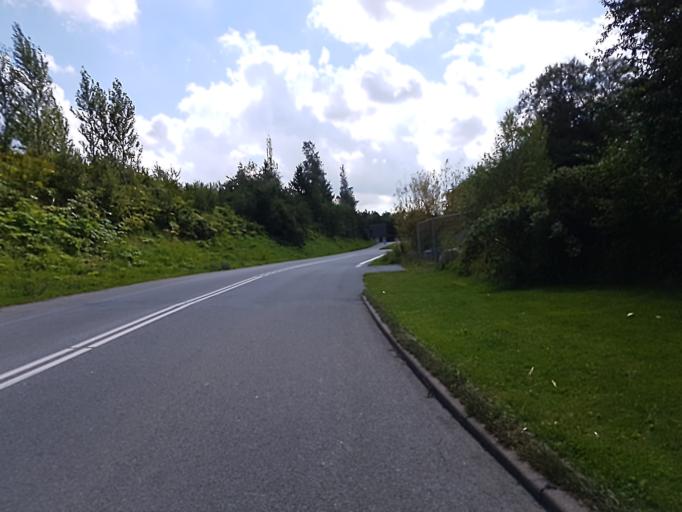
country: DK
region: Capital Region
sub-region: Egedal Kommune
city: Ganlose
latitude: 55.7810
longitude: 12.2684
